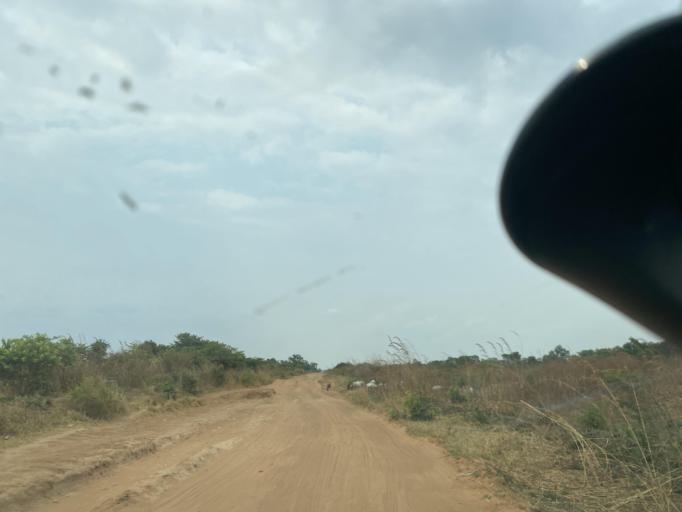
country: ZM
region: Lusaka
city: Lusaka
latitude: -15.2062
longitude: 28.3403
